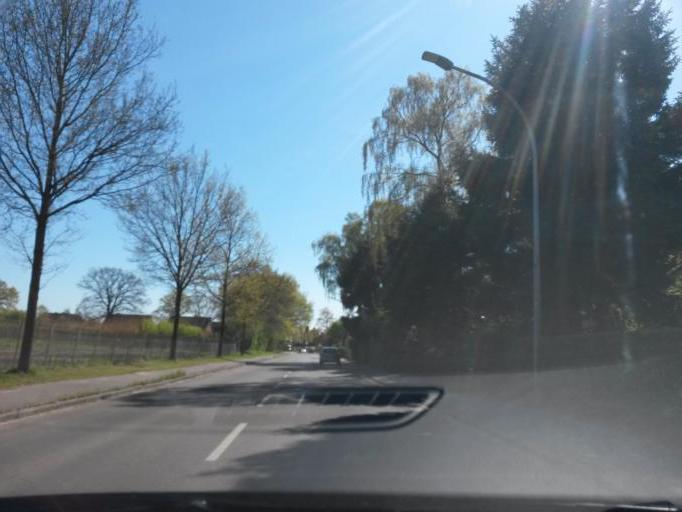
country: DE
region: Schleswig-Holstein
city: Rellingen
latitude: 53.6228
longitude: 9.8236
